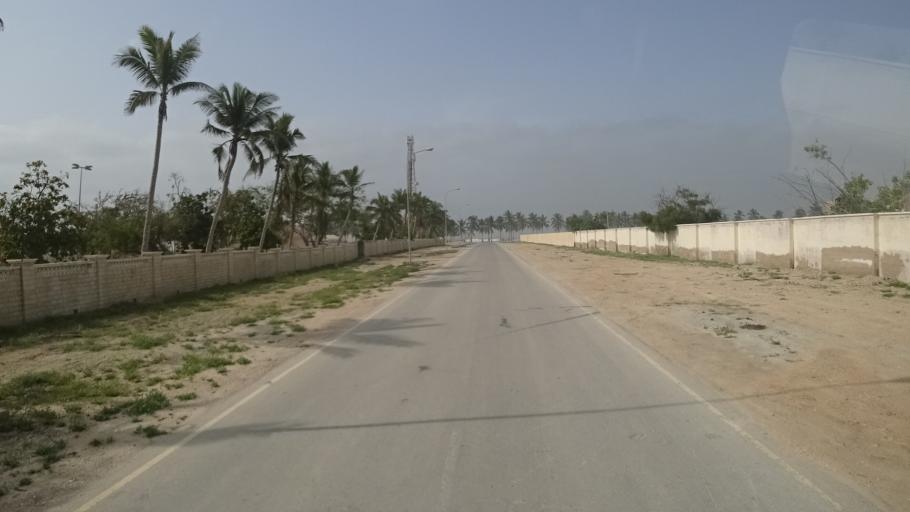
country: OM
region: Zufar
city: Salalah
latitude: 17.0134
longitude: 54.1706
